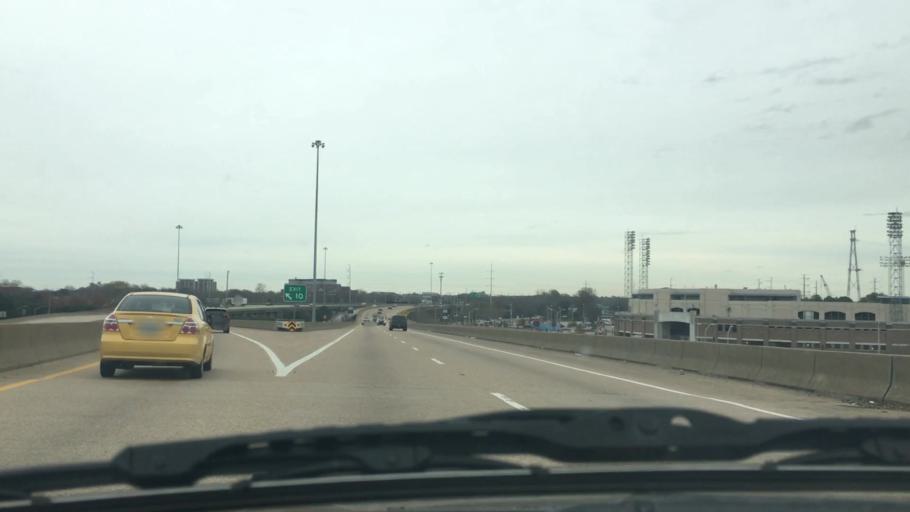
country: US
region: Virginia
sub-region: City of Norfolk
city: Norfolk
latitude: 36.8435
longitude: -76.2824
